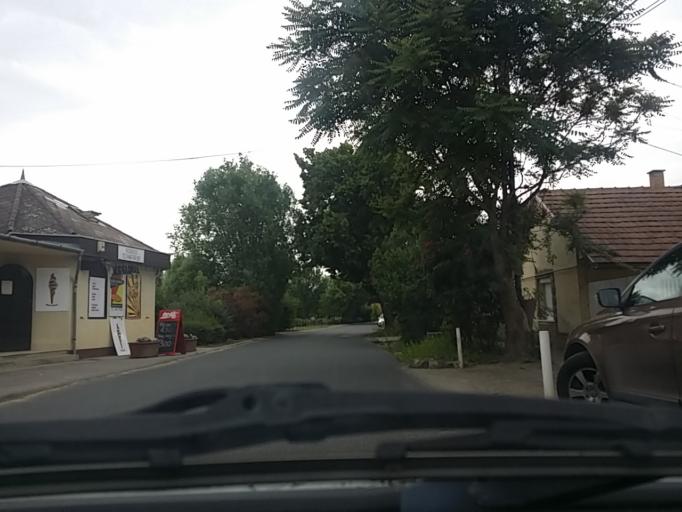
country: HU
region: Pest
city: Urom
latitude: 47.5983
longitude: 19.0146
